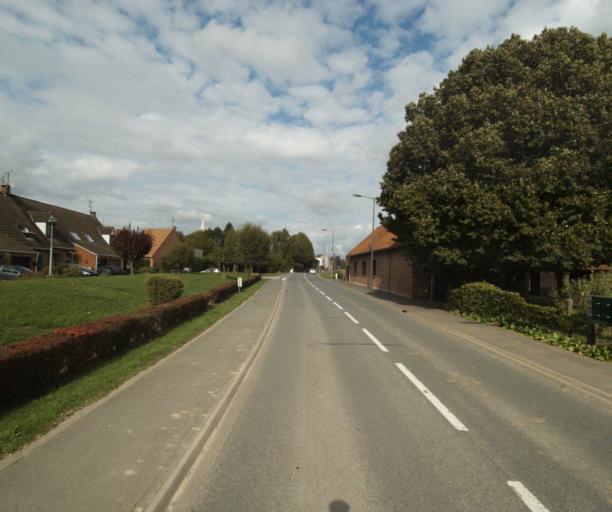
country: FR
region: Nord-Pas-de-Calais
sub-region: Departement du Nord
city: Premesques
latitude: 50.6529
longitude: 2.9507
